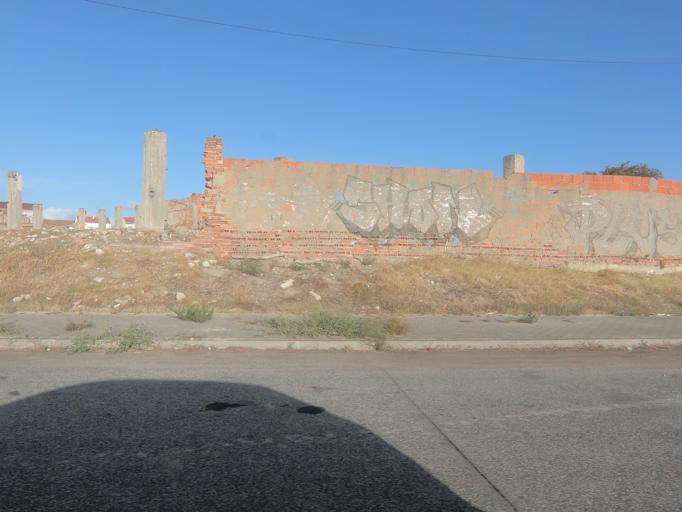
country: PT
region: Setubal
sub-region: Barreiro
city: Barreiro
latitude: 38.6685
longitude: -9.0572
